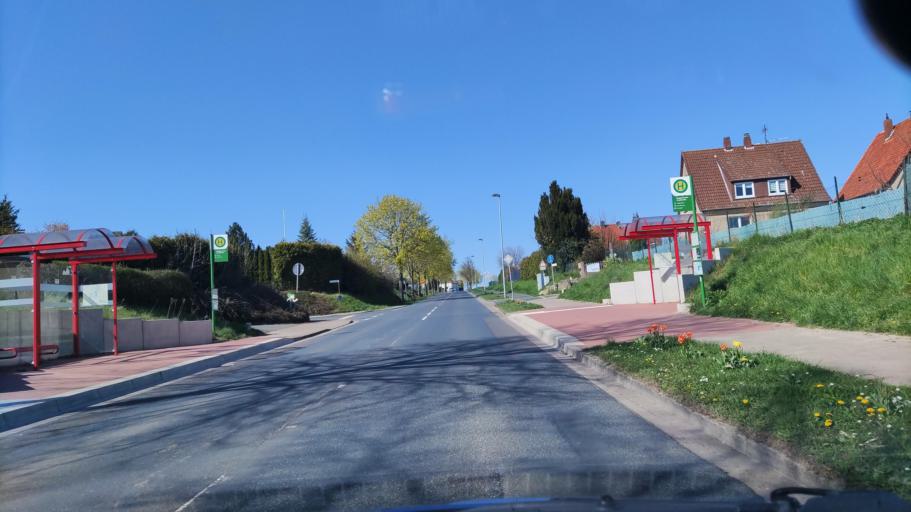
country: DE
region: Lower Saxony
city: Nordstemmen
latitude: 52.1457
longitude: 9.7755
